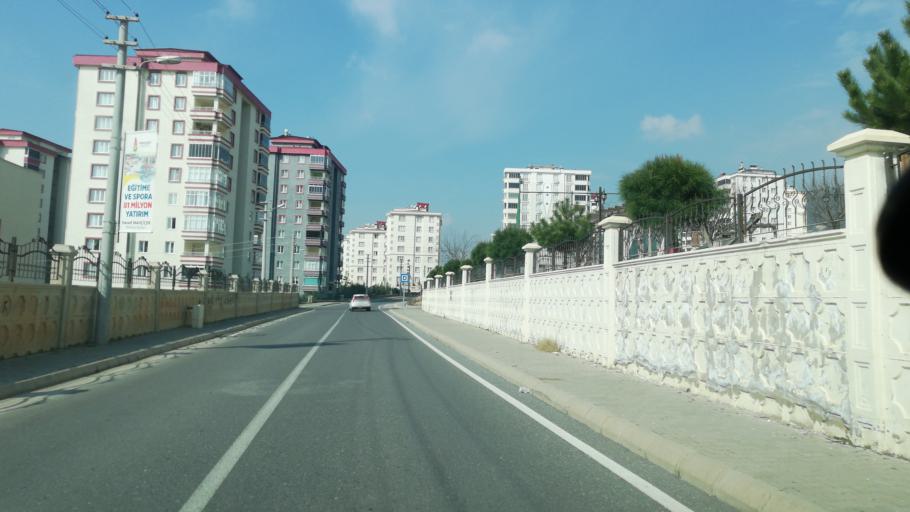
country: TR
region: Kahramanmaras
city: Kahramanmaras
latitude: 37.5897
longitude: 36.8602
